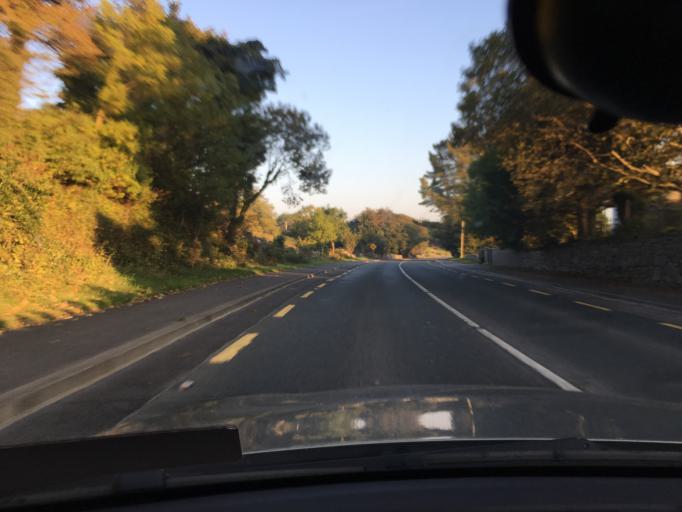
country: IE
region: Connaught
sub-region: County Galway
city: Oughterard
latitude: 53.3936
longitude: -9.2514
